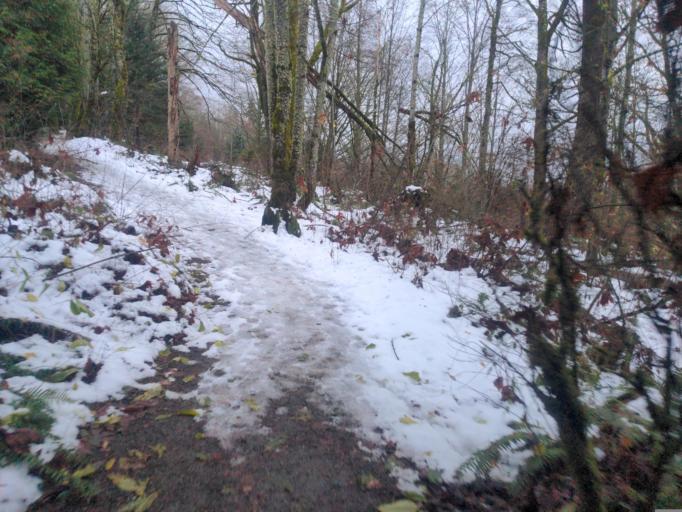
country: US
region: Washington
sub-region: King County
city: Eastgate
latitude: 47.5510
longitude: -122.1214
